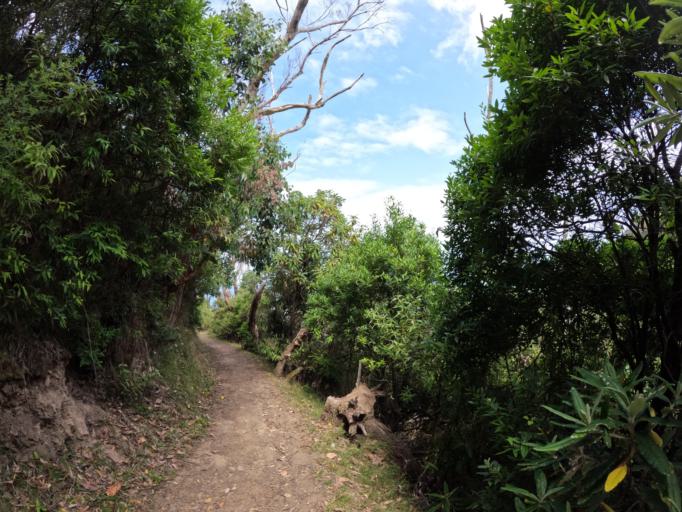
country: AU
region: Victoria
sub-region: Colac-Otway
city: Apollo Bay
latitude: -38.7909
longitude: 143.6221
